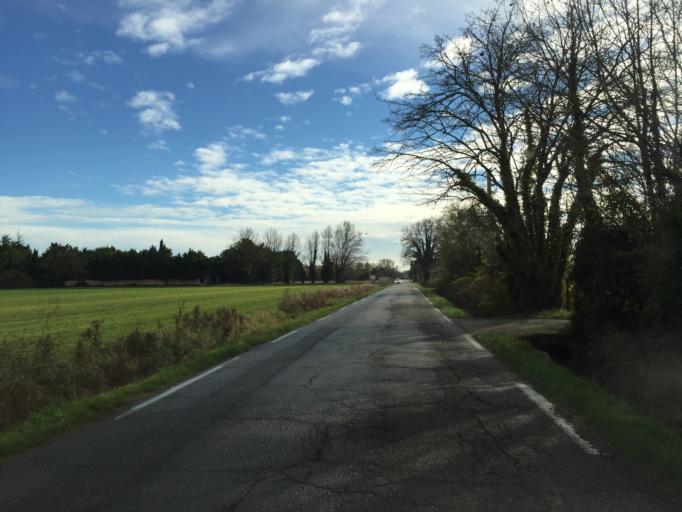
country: FR
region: Provence-Alpes-Cote d'Azur
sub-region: Departement du Vaucluse
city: Althen-des-Paluds
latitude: 43.9897
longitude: 4.9602
